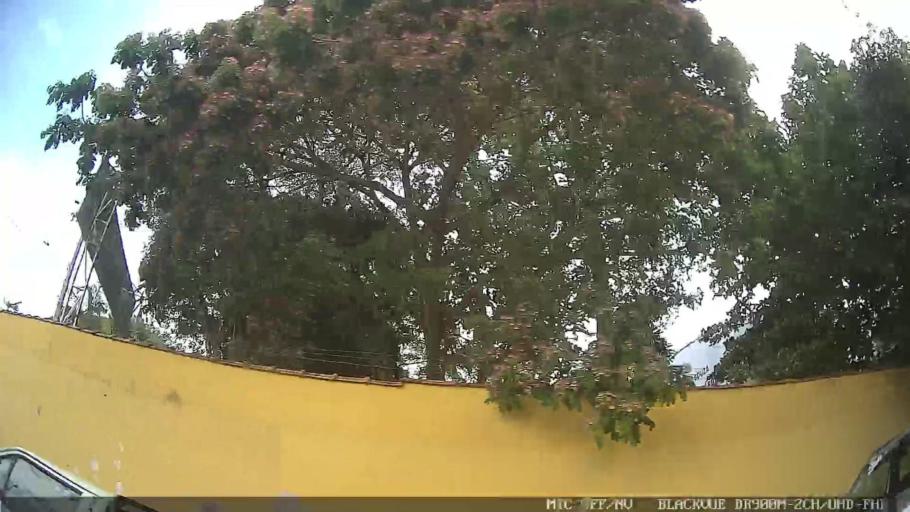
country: BR
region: Sao Paulo
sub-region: Amparo
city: Amparo
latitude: -22.7057
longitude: -46.7652
